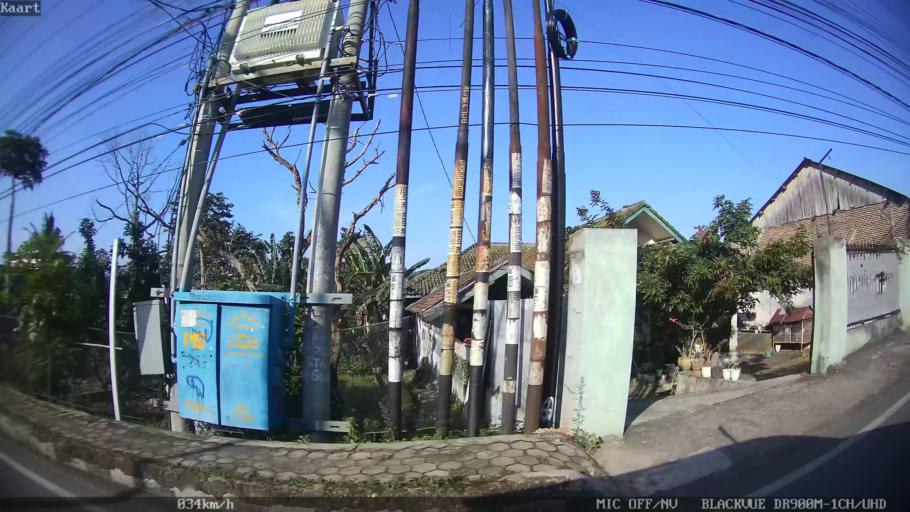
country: ID
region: Lampung
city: Kedaton
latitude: -5.3786
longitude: 105.2212
